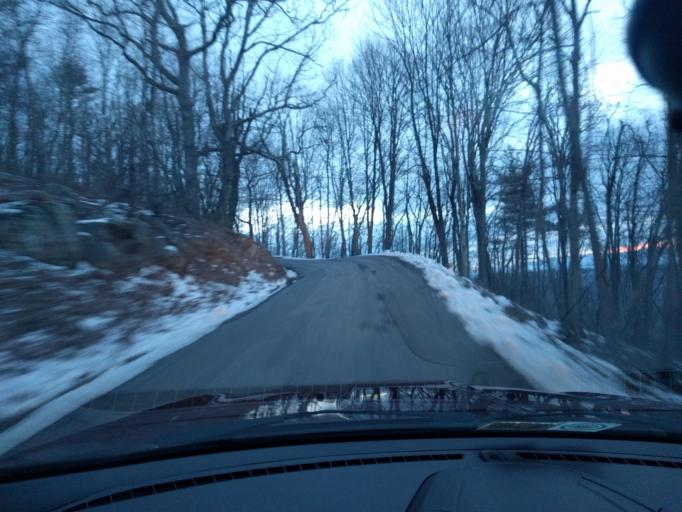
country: US
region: Virginia
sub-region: Alleghany County
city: Clifton Forge
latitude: 37.8711
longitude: -79.8875
